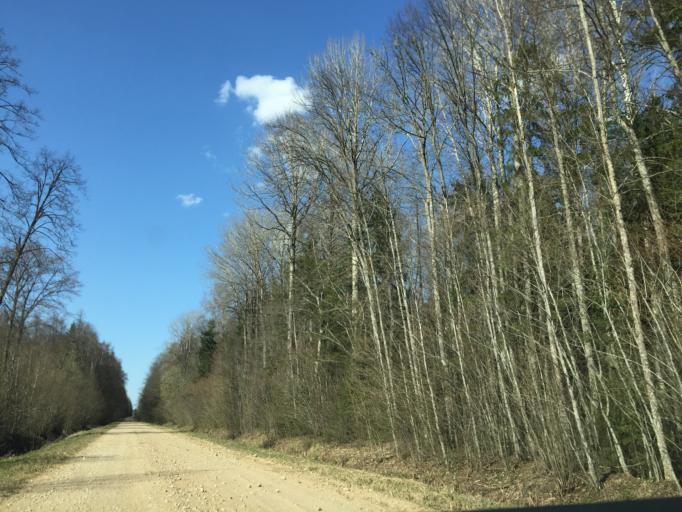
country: LV
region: Kegums
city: Kegums
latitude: 56.8612
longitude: 24.8017
